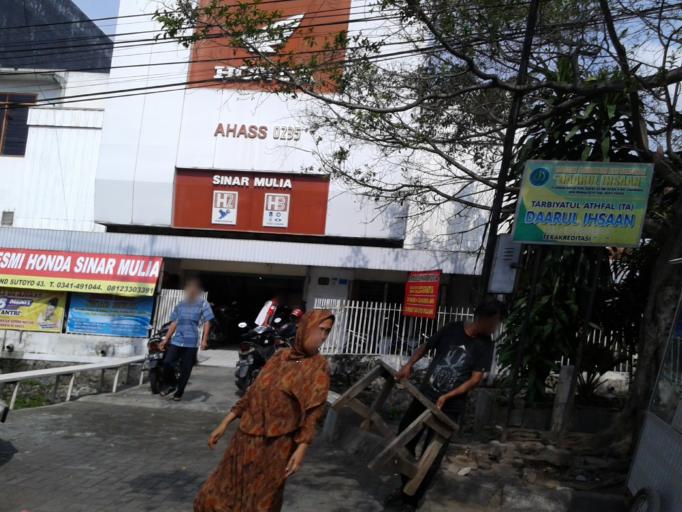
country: ID
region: East Java
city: Malang
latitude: -7.9653
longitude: 112.6336
